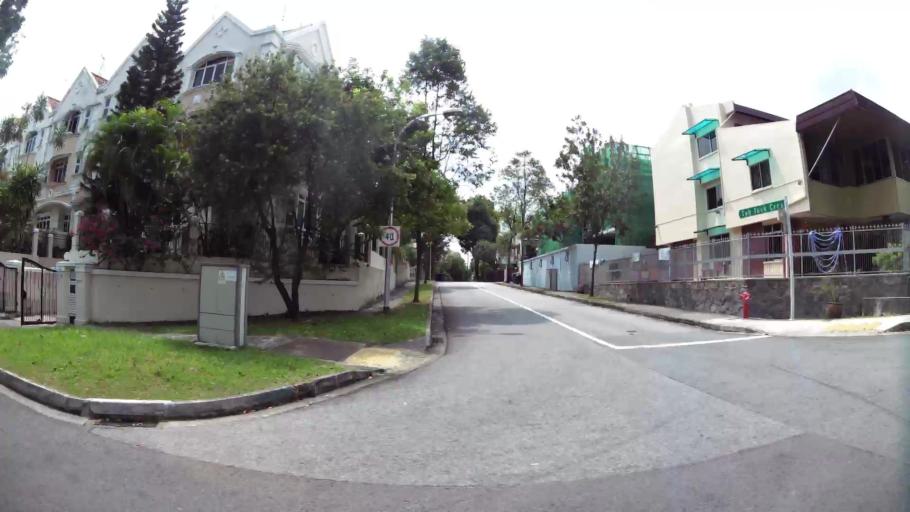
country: SG
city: Singapore
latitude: 1.3397
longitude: 103.7659
